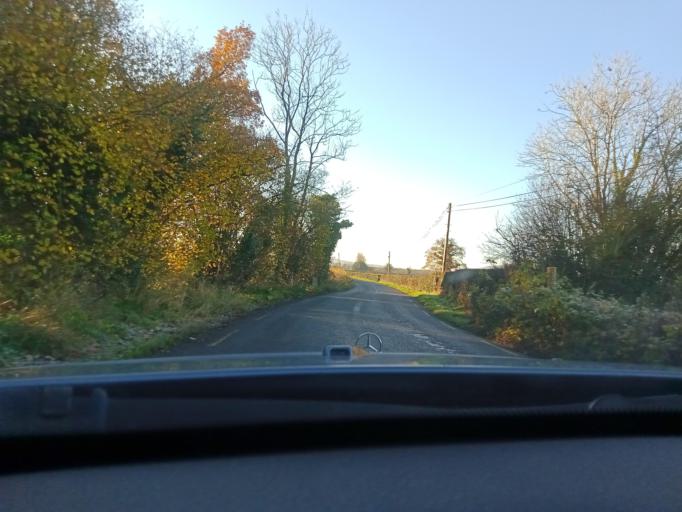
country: IE
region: Leinster
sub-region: Kilkenny
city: Callan
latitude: 52.5177
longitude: -7.3847
